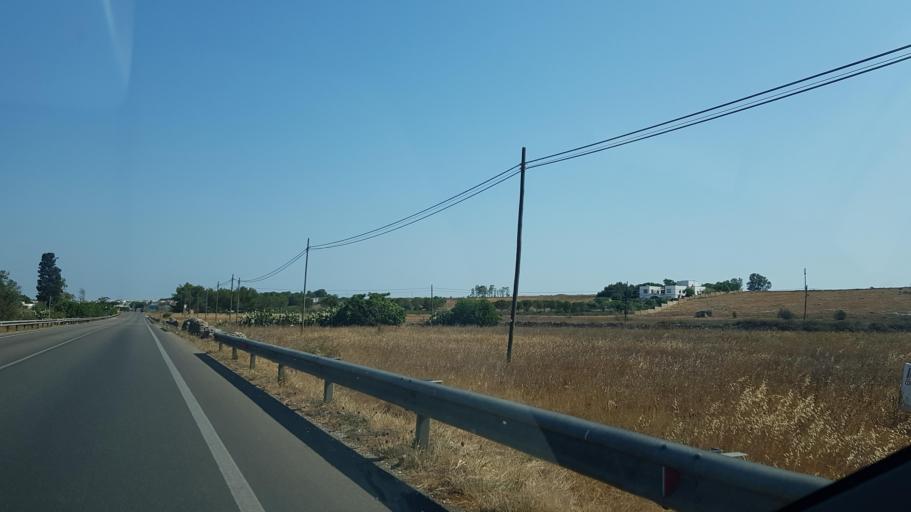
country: IT
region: Apulia
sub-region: Provincia di Lecce
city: Nociglia
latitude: 40.0245
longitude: 18.3248
